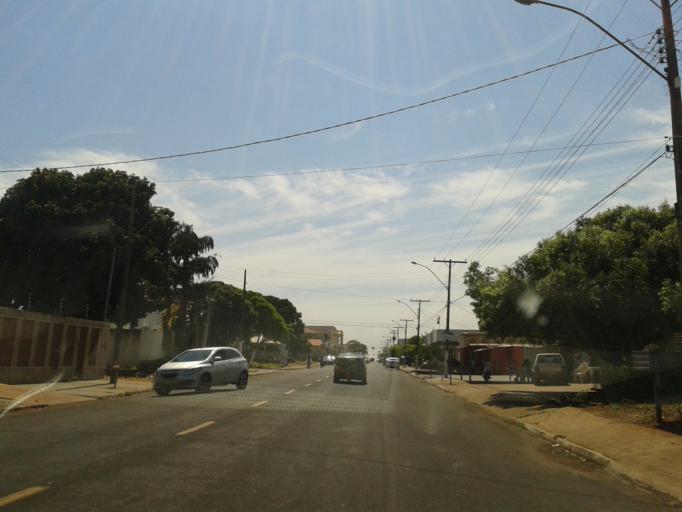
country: BR
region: Minas Gerais
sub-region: Santa Vitoria
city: Santa Vitoria
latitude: -18.9986
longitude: -50.5499
